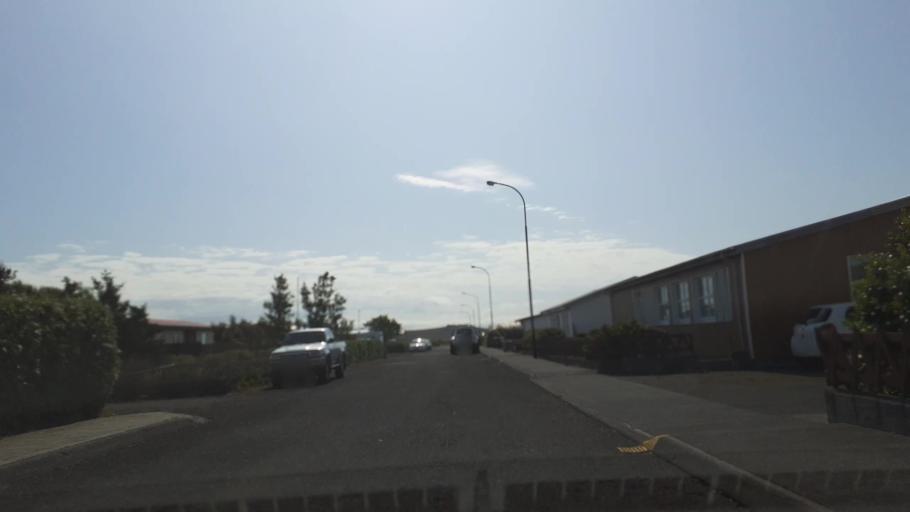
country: IS
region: Northwest
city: Saudarkrokur
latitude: 65.8223
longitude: -20.3004
